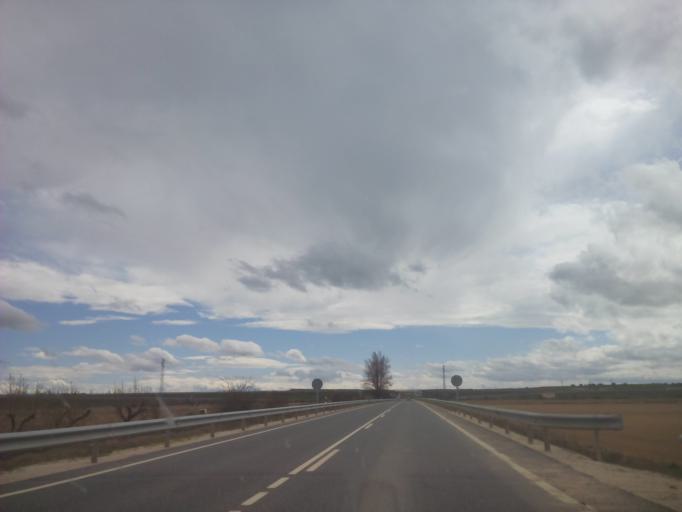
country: ES
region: Castille and Leon
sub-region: Provincia de Salamanca
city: Machacon
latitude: 40.9278
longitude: -5.5040
